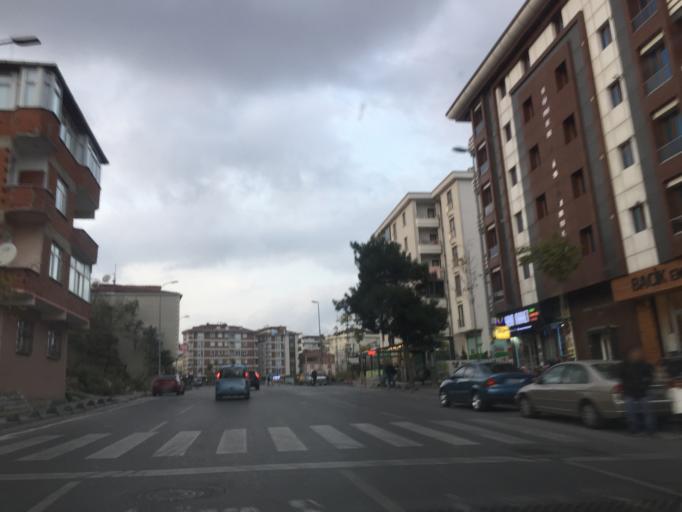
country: TR
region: Istanbul
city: Samandira
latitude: 40.9881
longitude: 29.2317
